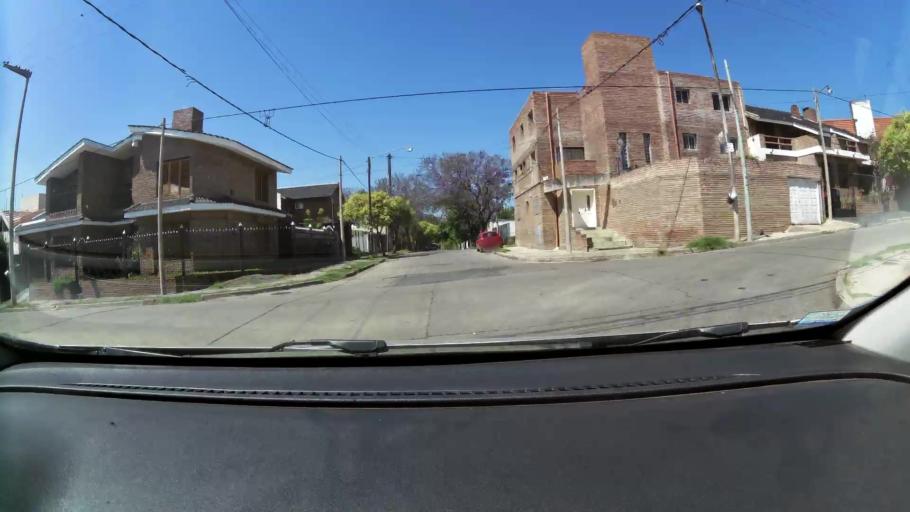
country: AR
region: Cordoba
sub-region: Departamento de Capital
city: Cordoba
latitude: -31.4269
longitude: -64.2034
